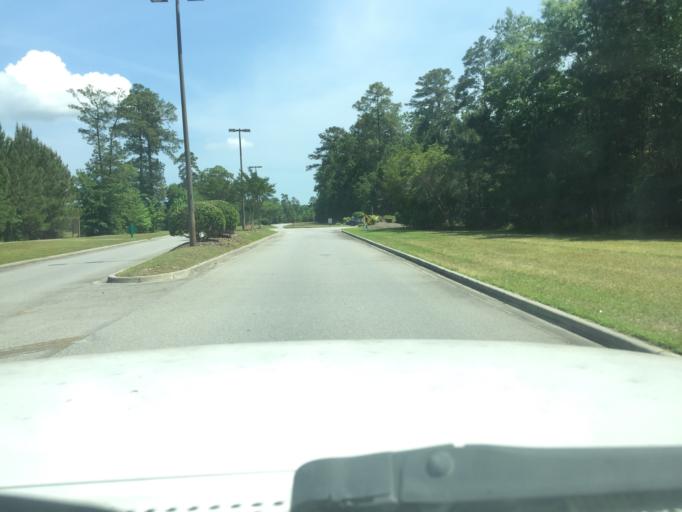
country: US
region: Georgia
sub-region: Chatham County
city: Georgetown
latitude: 32.0392
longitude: -81.2337
